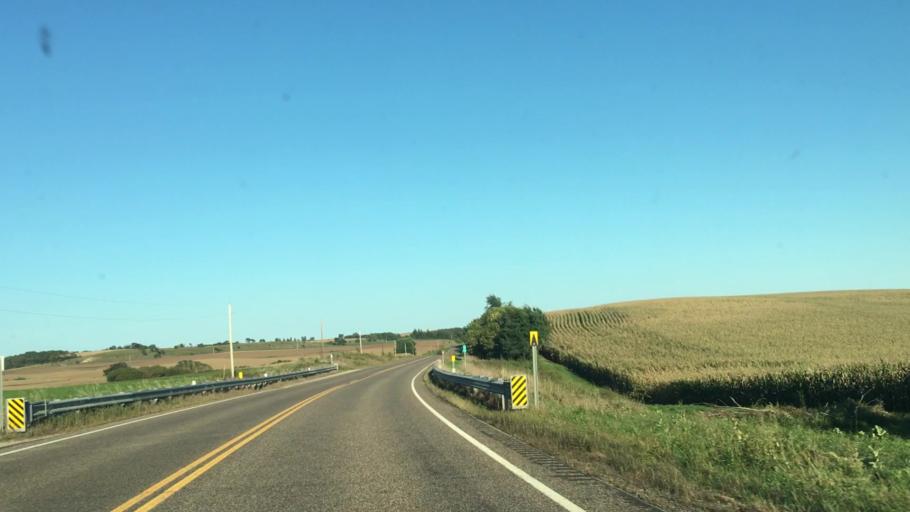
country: US
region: Minnesota
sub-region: Fillmore County
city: Chatfield
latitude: 43.8542
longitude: -92.1342
